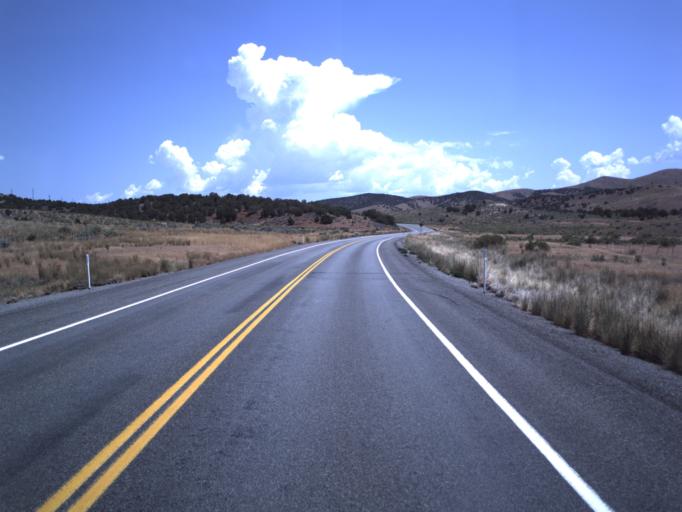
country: US
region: Utah
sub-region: Juab County
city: Nephi
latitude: 39.5893
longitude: -112.1631
